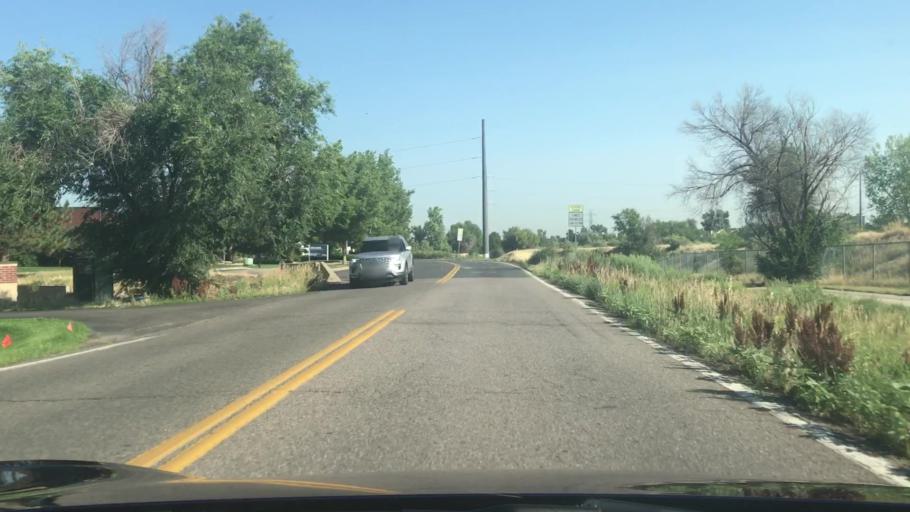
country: US
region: Colorado
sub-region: Arapahoe County
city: Glendale
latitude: 39.6782
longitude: -104.8960
